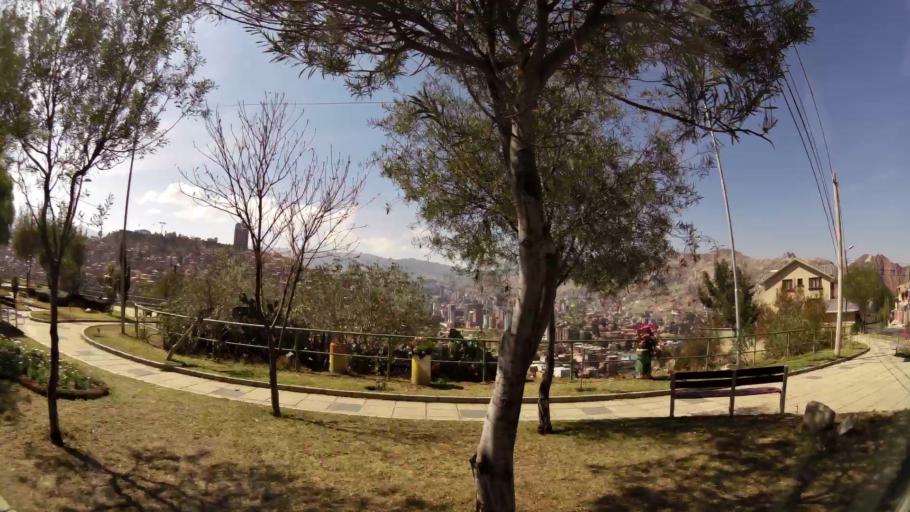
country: BO
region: La Paz
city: La Paz
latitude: -16.5389
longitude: -68.0987
